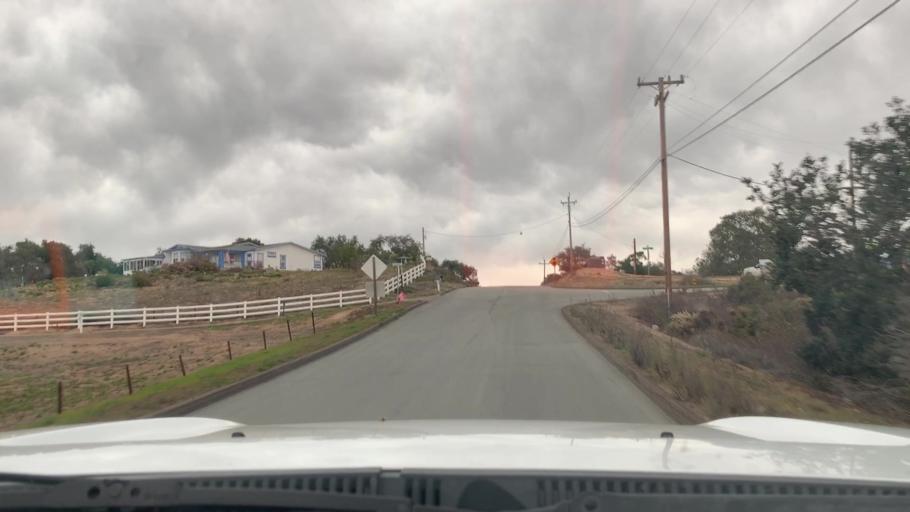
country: US
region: California
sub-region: San Luis Obispo County
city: Callender
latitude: 35.0663
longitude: -120.5603
